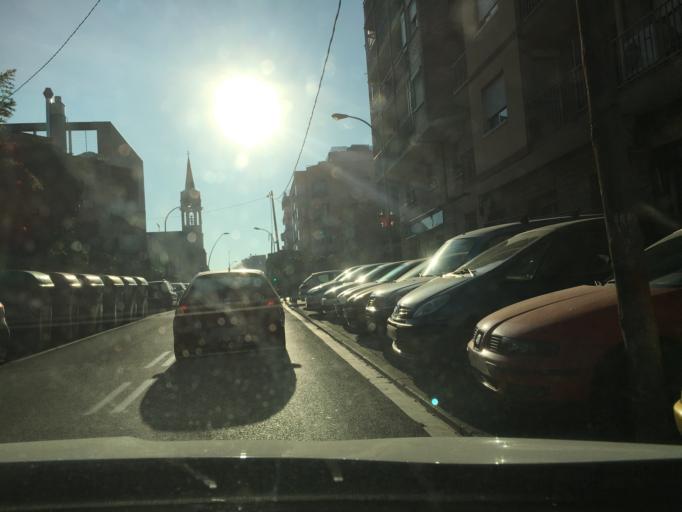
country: ES
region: Catalonia
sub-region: Provincia de Barcelona
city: Santa Coloma de Gramenet
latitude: 41.4546
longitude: 2.2105
